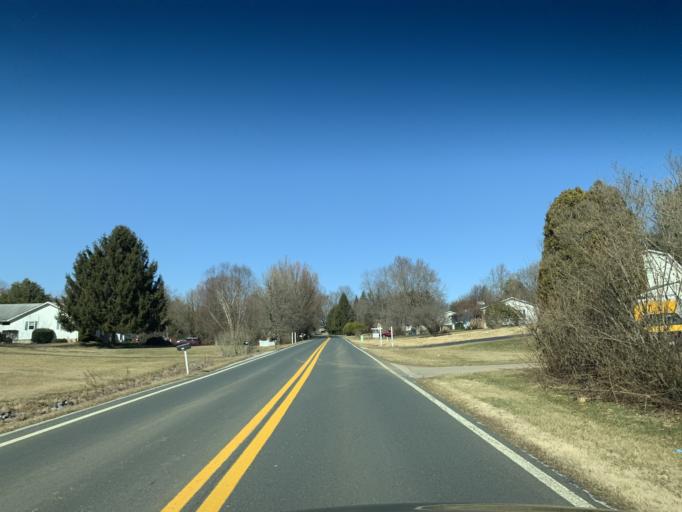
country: US
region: Maryland
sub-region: Carroll County
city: Hampstead
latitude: 39.5767
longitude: -76.8973
